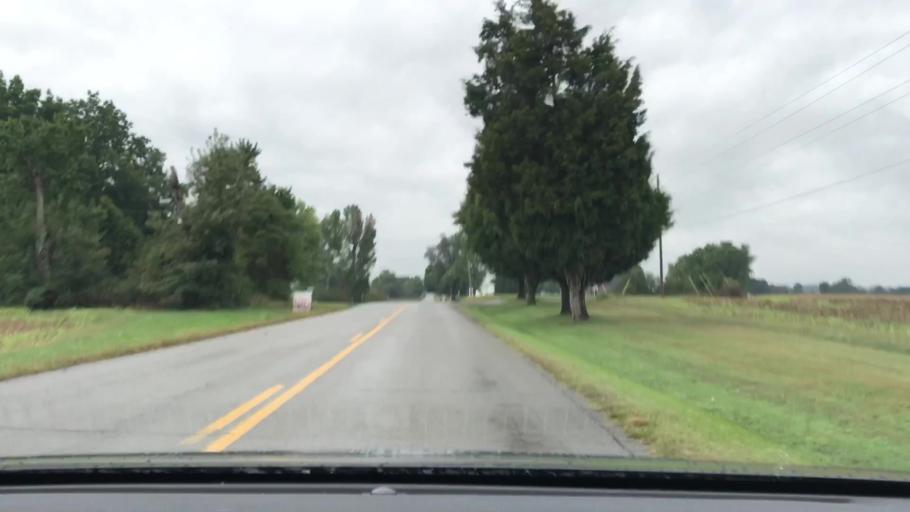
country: US
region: Kentucky
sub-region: McLean County
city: Calhoun
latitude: 37.4456
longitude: -87.2445
